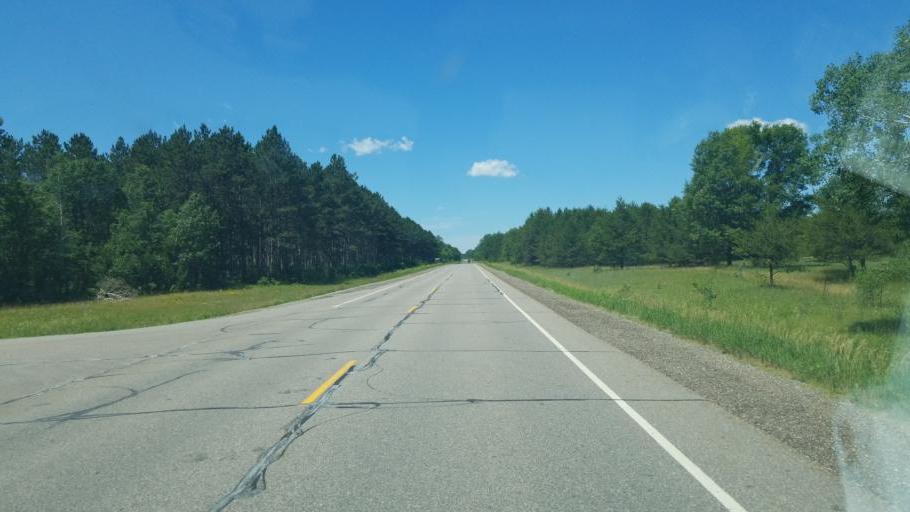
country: US
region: Wisconsin
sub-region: Adams County
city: Friendship
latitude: 44.0470
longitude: -89.9954
